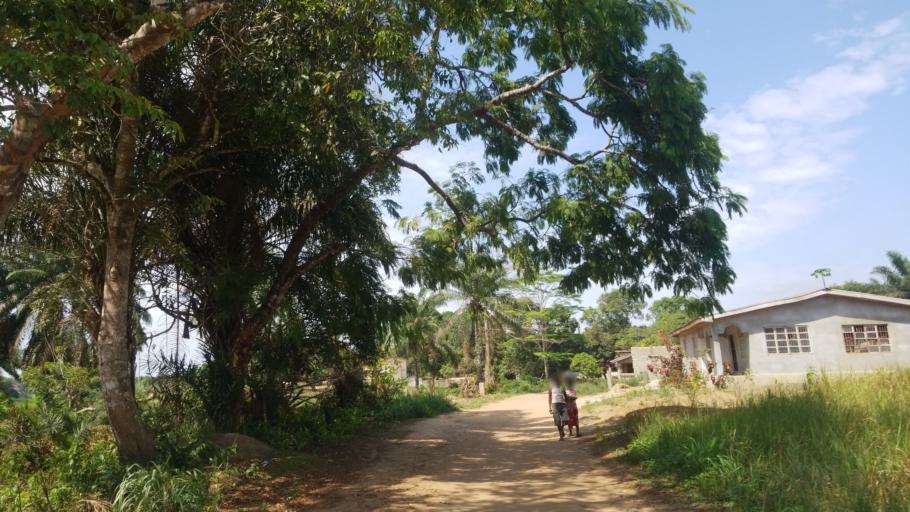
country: SL
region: Western Area
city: Waterloo
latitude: 8.3225
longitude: -13.0307
